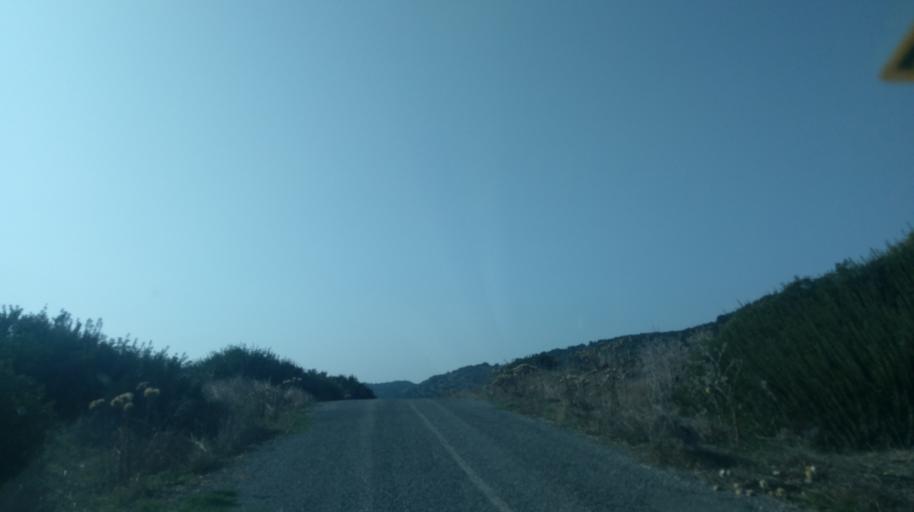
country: CY
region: Ammochostos
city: Rizokarpaso
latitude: 35.5518
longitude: 34.3589
